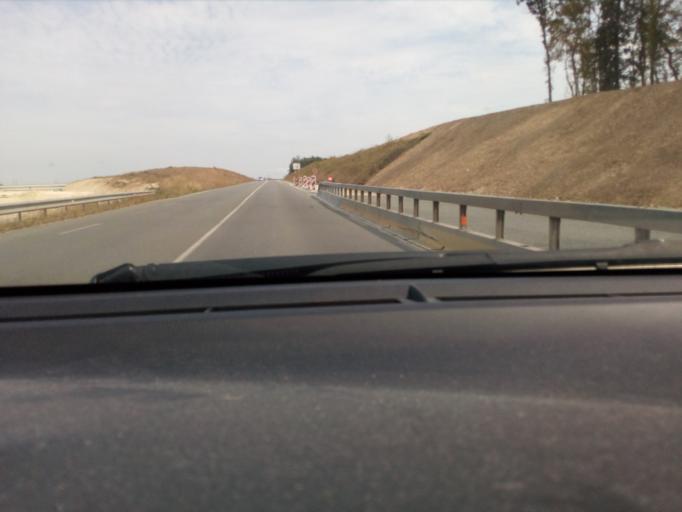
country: FR
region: Poitou-Charentes
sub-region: Departement de la Charente
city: Saint-Saturnin
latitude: 45.6805
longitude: 0.0657
